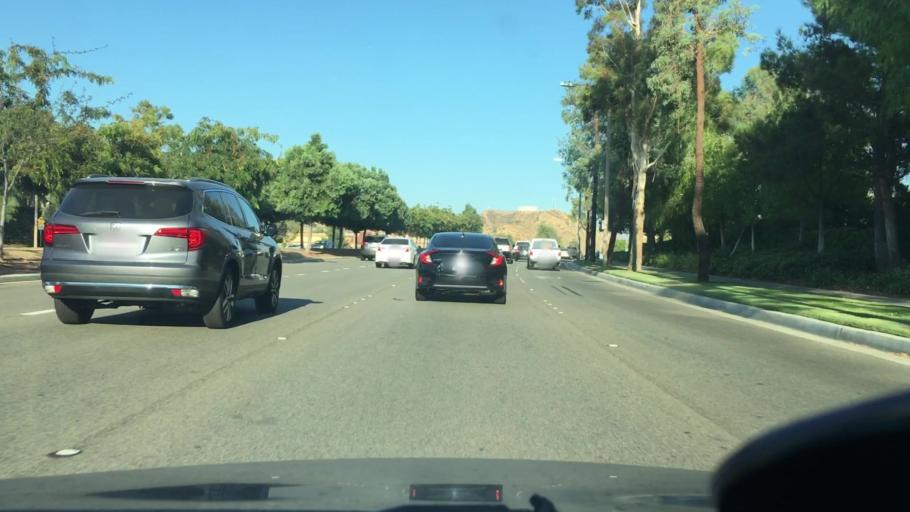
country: US
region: California
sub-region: Los Angeles County
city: Santa Clarita
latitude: 34.4283
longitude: -118.5418
